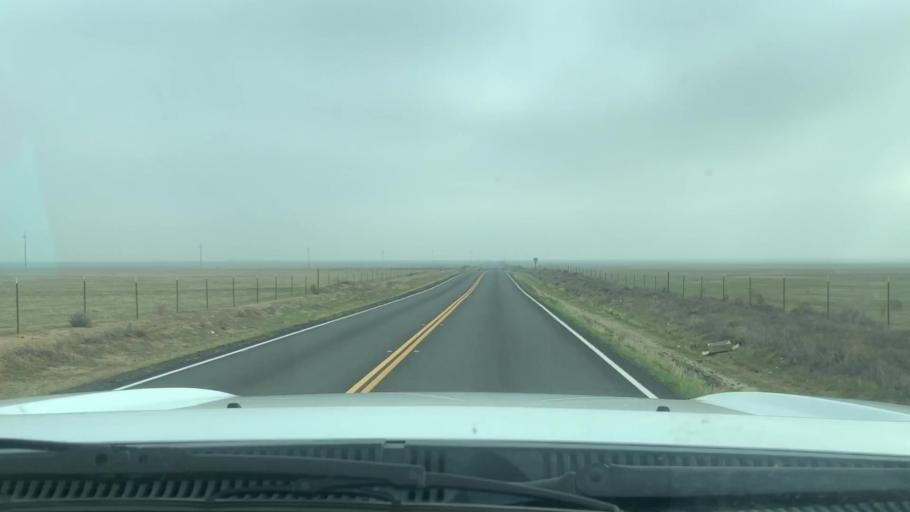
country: US
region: California
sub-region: Kern County
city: Lost Hills
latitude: 35.5957
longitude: -119.8441
